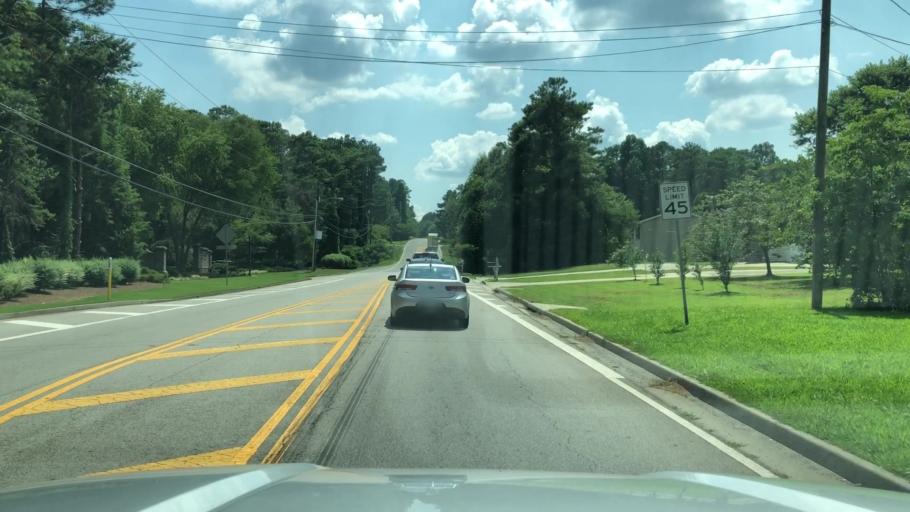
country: US
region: Georgia
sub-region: Cobb County
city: Acworth
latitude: 33.9904
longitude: -84.7103
